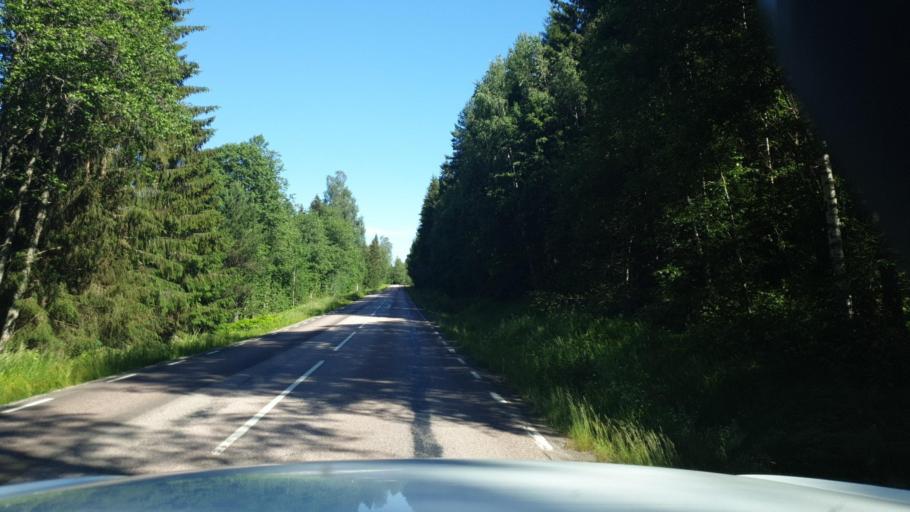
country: SE
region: Vaermland
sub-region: Eda Kommun
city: Amotfors
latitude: 59.8617
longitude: 12.5460
